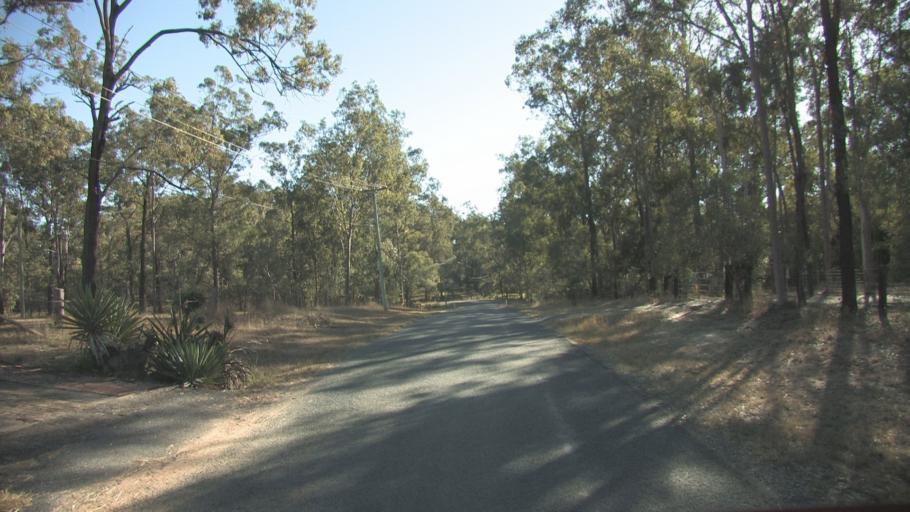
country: AU
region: Queensland
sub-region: Logan
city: North Maclean
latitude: -27.7810
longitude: 152.9652
